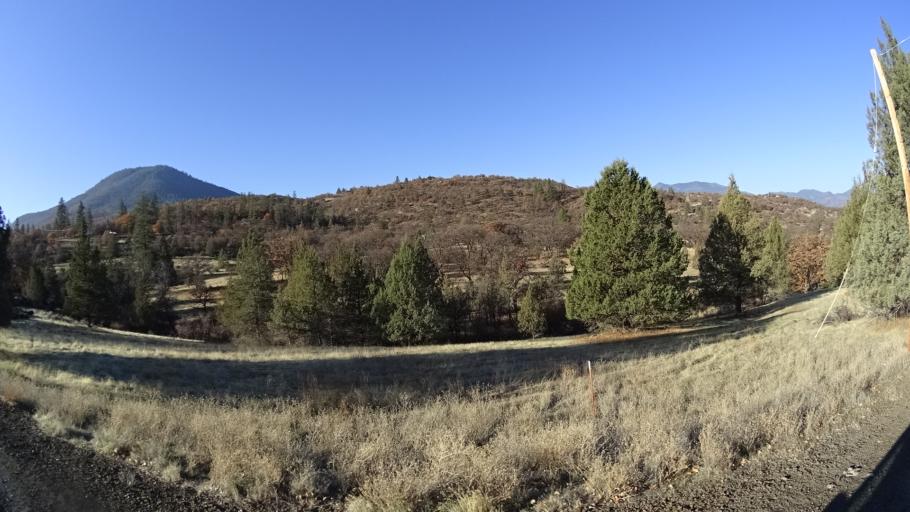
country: US
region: California
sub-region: Siskiyou County
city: Montague
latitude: 41.8924
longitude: -122.4983
